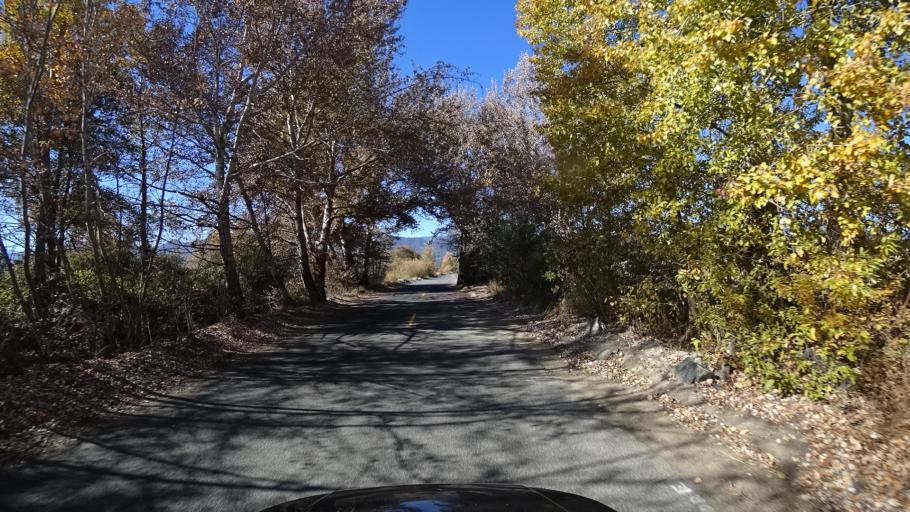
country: US
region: California
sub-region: Siskiyou County
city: Yreka
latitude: 41.5148
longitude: -122.8715
